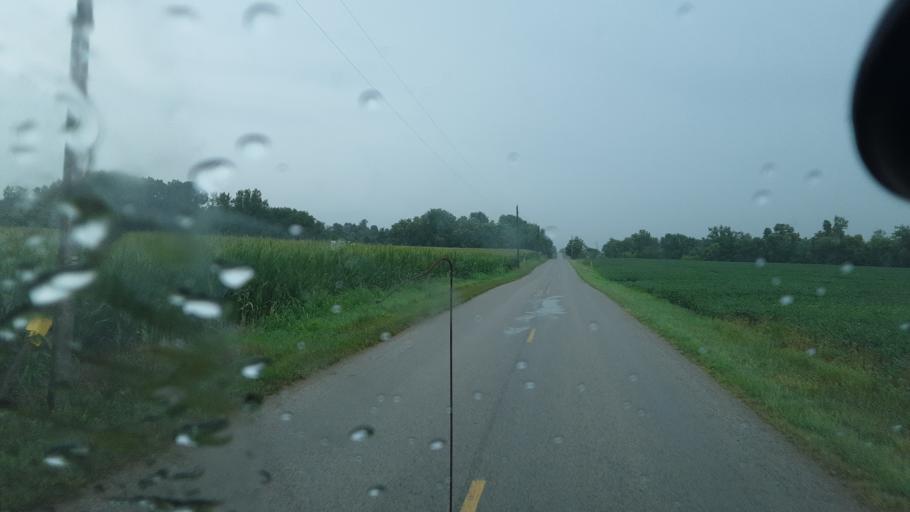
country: US
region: Ohio
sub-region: Williams County
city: Edgerton
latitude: 41.4695
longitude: -84.8141
